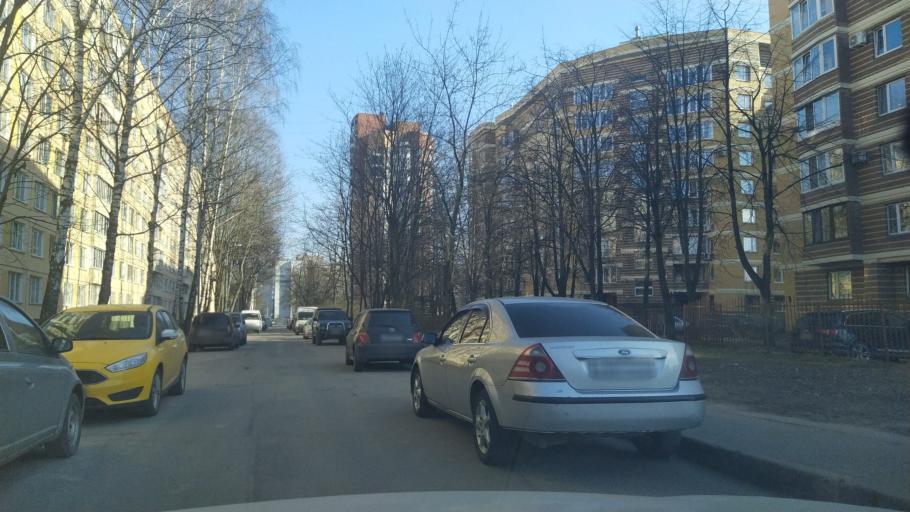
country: RU
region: Leningrad
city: Akademicheskoe
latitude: 60.0182
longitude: 30.3978
